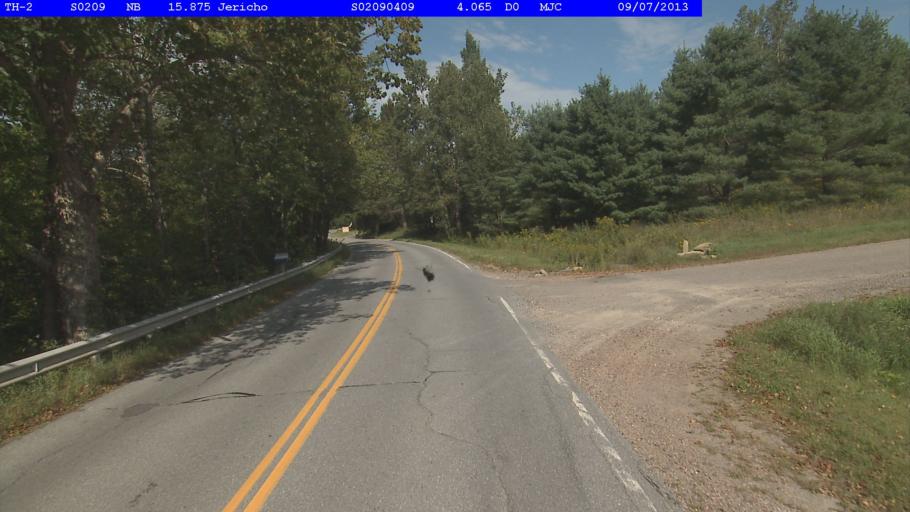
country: US
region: Vermont
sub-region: Chittenden County
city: Jericho
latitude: 44.4831
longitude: -72.9742
